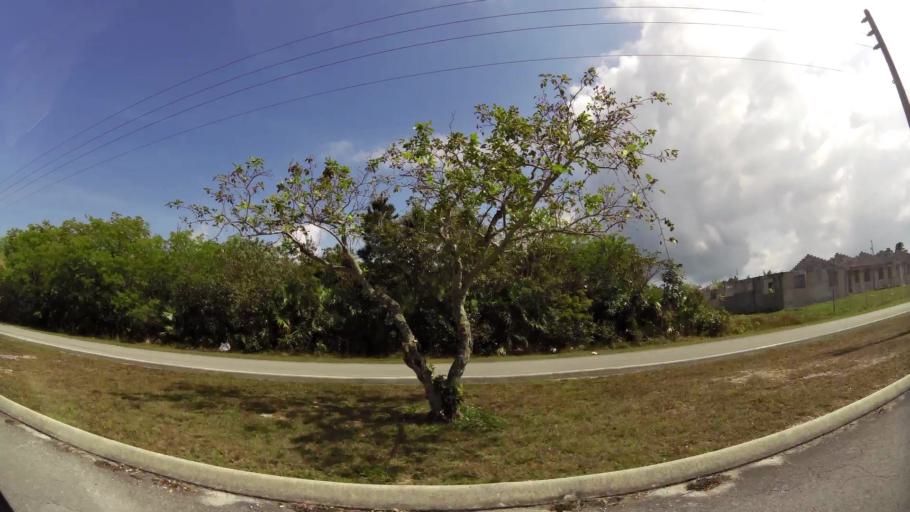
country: BS
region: Freeport
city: Freeport
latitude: 26.5046
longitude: -78.7073
